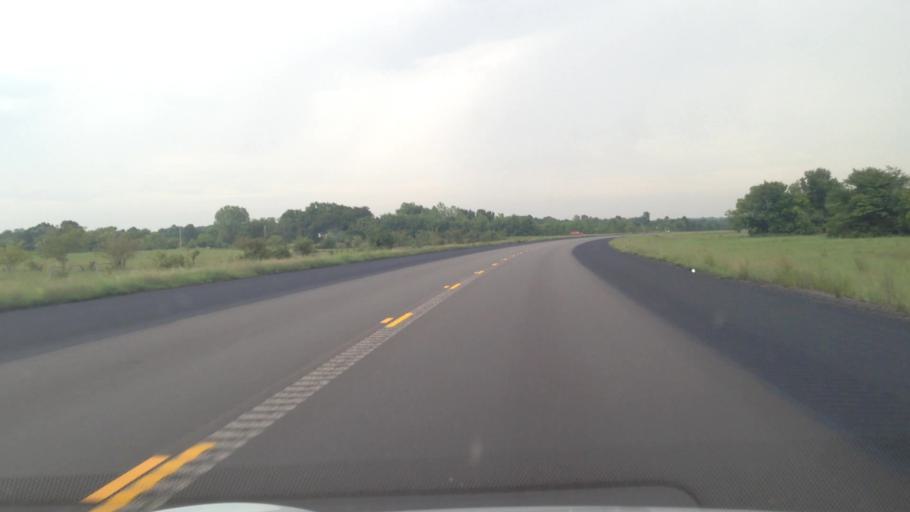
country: US
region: Kansas
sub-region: Cherokee County
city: Baxter Springs
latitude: 37.0477
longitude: -94.7147
